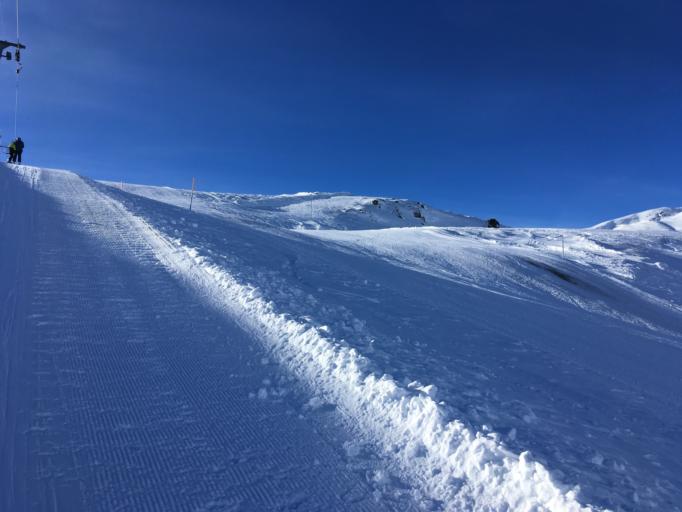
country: CH
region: Grisons
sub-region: Maloja District
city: Promontogno
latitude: 46.4547
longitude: 9.6455
